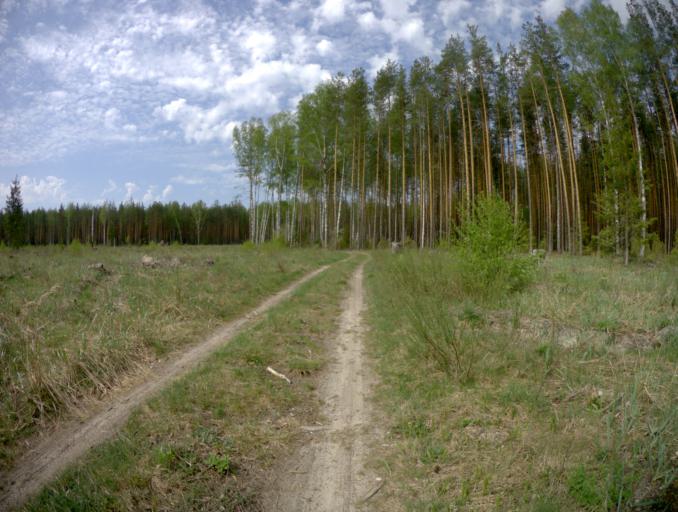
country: RU
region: Ivanovo
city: Yuzha
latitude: 56.4863
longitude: 42.1525
